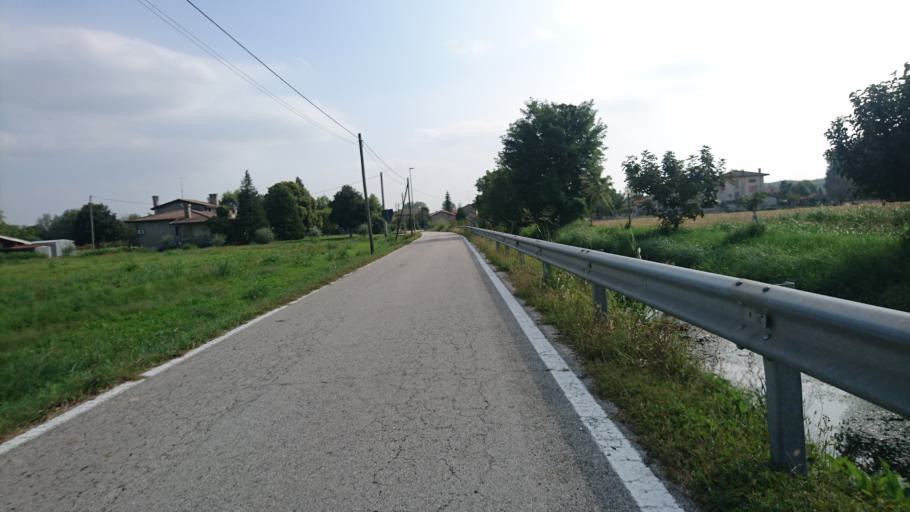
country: IT
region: Veneto
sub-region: Provincia di Padova
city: San Giorgio in Bosco
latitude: 45.5815
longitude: 11.7712
